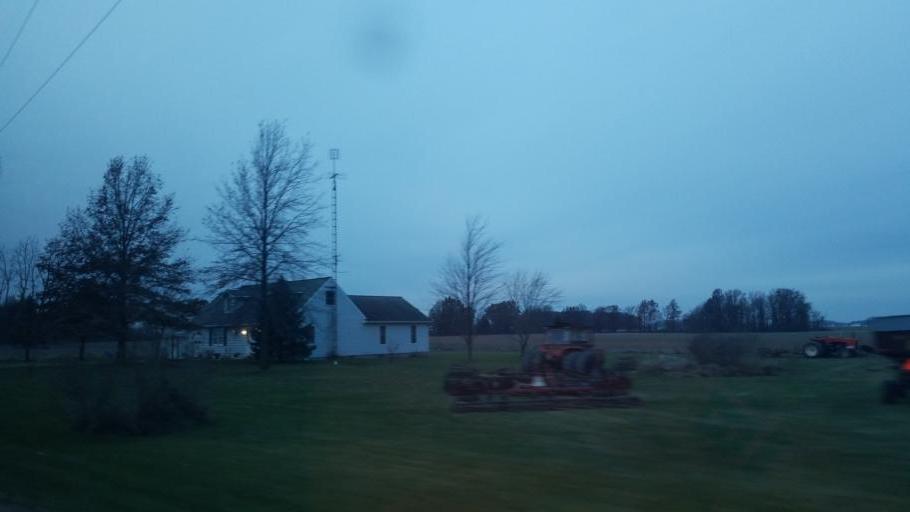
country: US
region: Indiana
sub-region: Adams County
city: Berne
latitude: 40.7303
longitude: -84.9789
